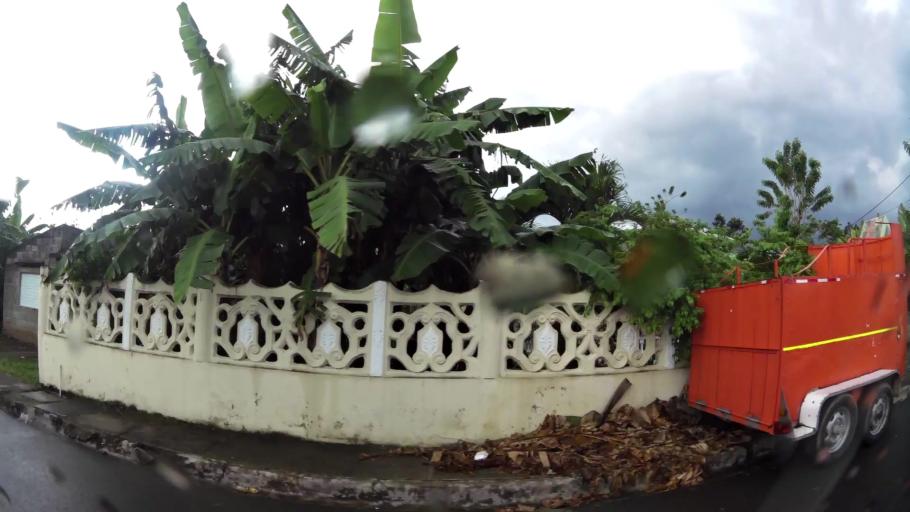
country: DO
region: Monsenor Nouel
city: Bonao
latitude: 18.9353
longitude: -70.3989
